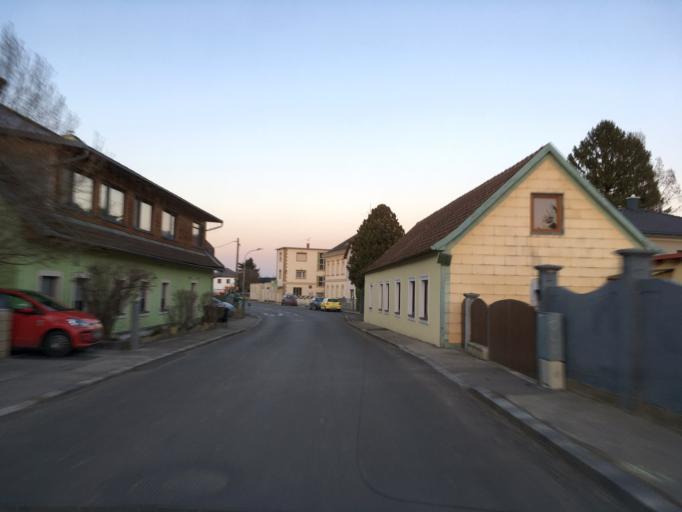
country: AT
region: Lower Austria
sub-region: Politischer Bezirk Tulln
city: Wordern
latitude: 48.3293
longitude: 16.2106
